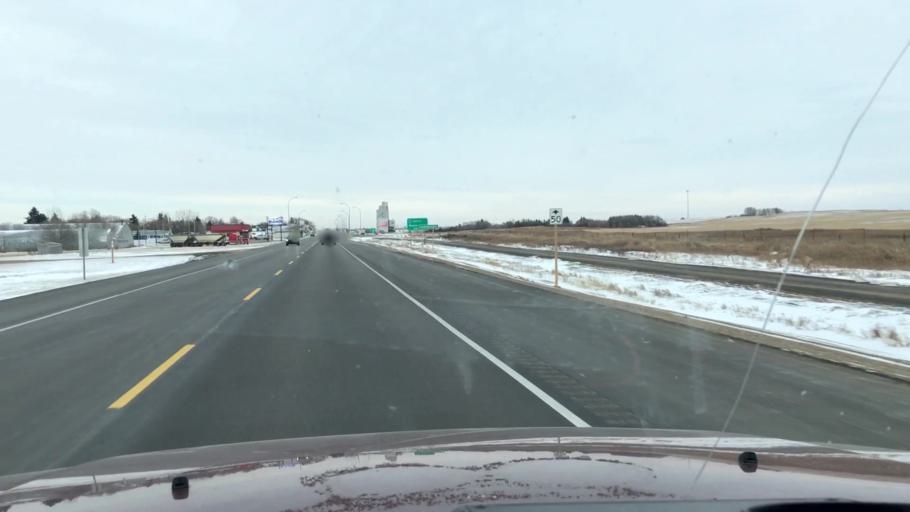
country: CA
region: Saskatchewan
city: Moose Jaw
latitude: 50.8546
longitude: -105.5751
